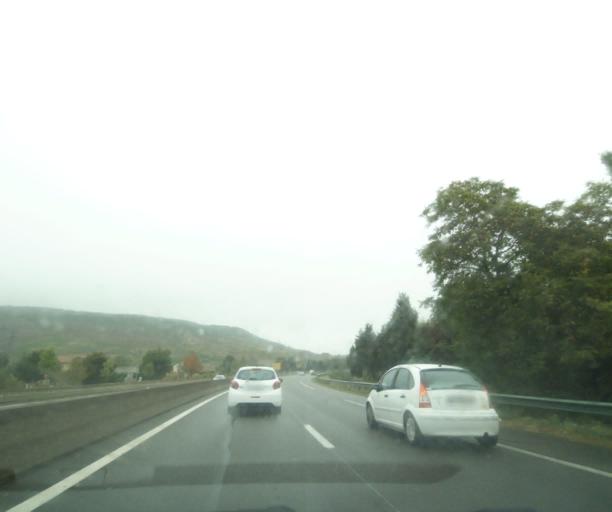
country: FR
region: Auvergne
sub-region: Departement du Puy-de-Dome
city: Cebazat
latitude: 45.8496
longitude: 3.1130
